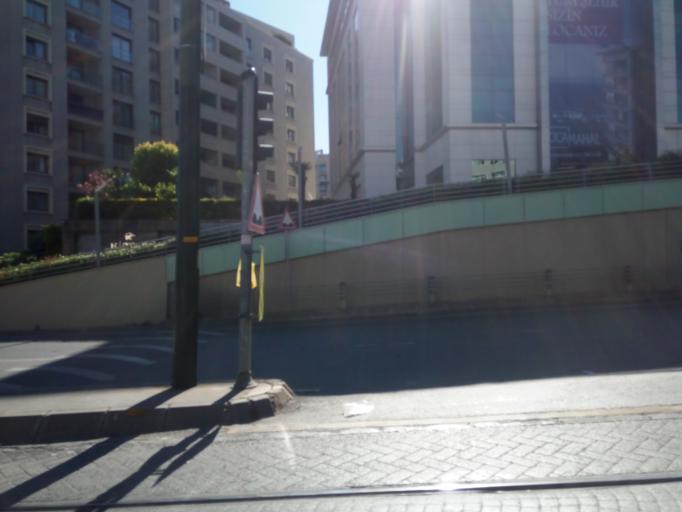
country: TR
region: Istanbul
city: Zeytinburnu
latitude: 41.0091
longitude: 28.9095
